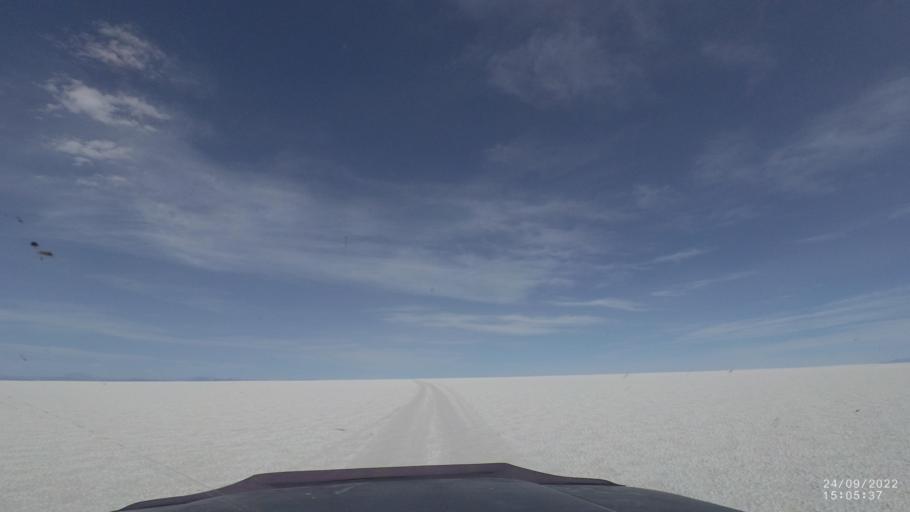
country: BO
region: Potosi
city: Colchani
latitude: -19.9075
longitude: -67.5160
